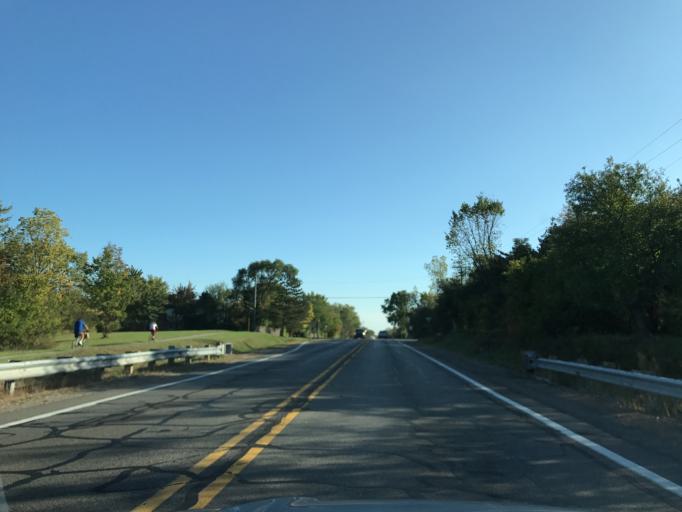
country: US
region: Michigan
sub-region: Oakland County
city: Farmington Hills
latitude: 42.4771
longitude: -83.3381
